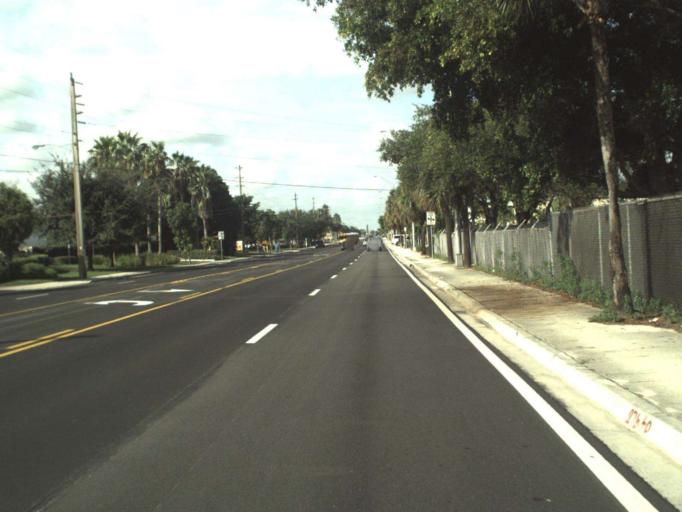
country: US
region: Florida
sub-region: Miami-Dade County
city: North Miami Beach
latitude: 25.9210
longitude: -80.1573
